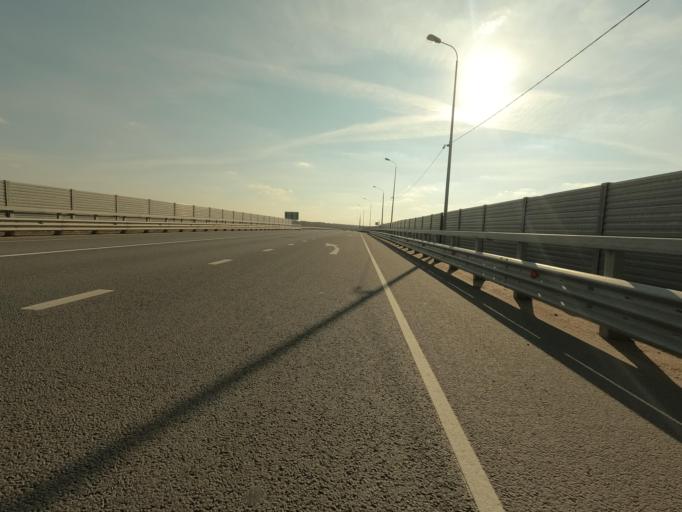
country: RU
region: Leningrad
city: Mga
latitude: 59.7549
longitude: 31.0920
